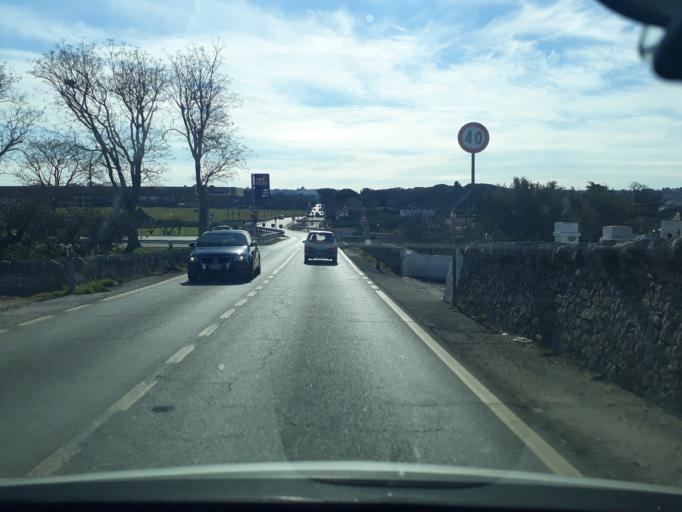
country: IT
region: Apulia
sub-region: Provincia di Bari
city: Locorotondo
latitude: 40.7379
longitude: 17.3325
